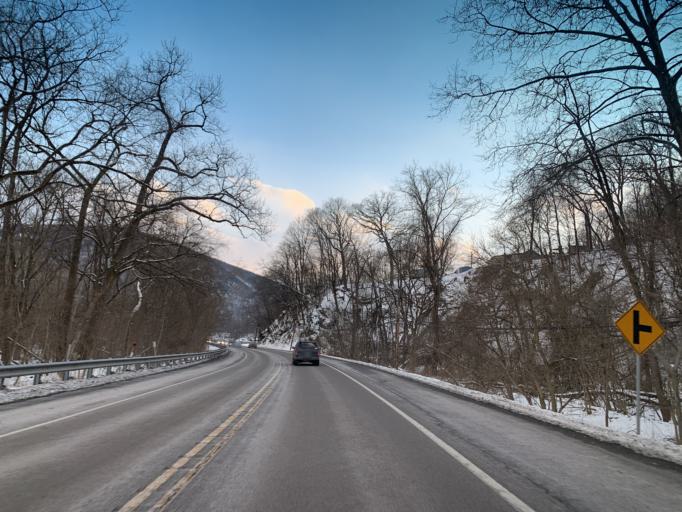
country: US
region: Maryland
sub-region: Allegany County
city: La Vale
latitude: 39.6783
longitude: -78.7915
